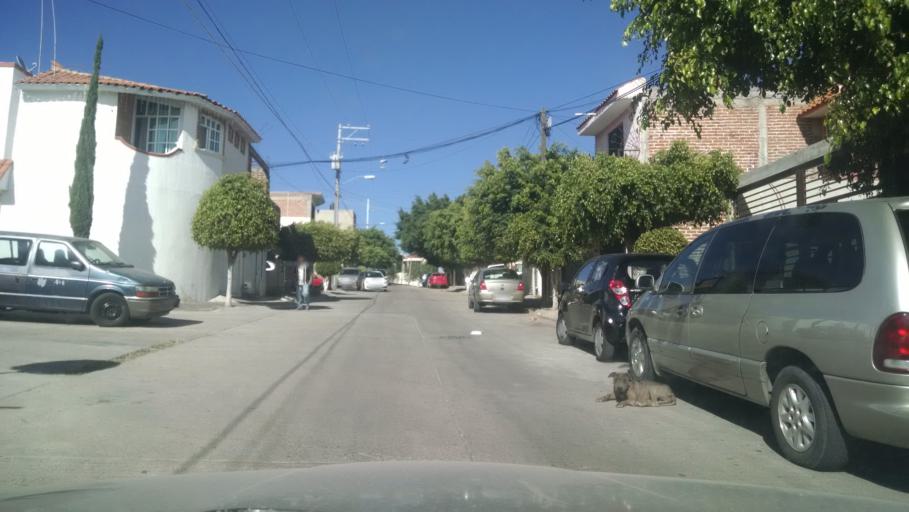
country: MX
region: Guanajuato
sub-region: Leon
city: Ejido la Joya
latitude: 21.1212
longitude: -101.7258
